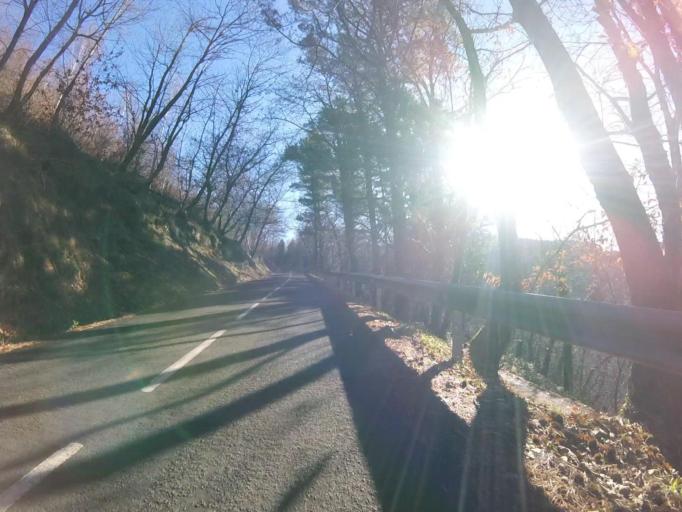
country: ES
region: Basque Country
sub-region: Provincia de Guipuzcoa
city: Irun
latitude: 43.3155
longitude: -1.7618
